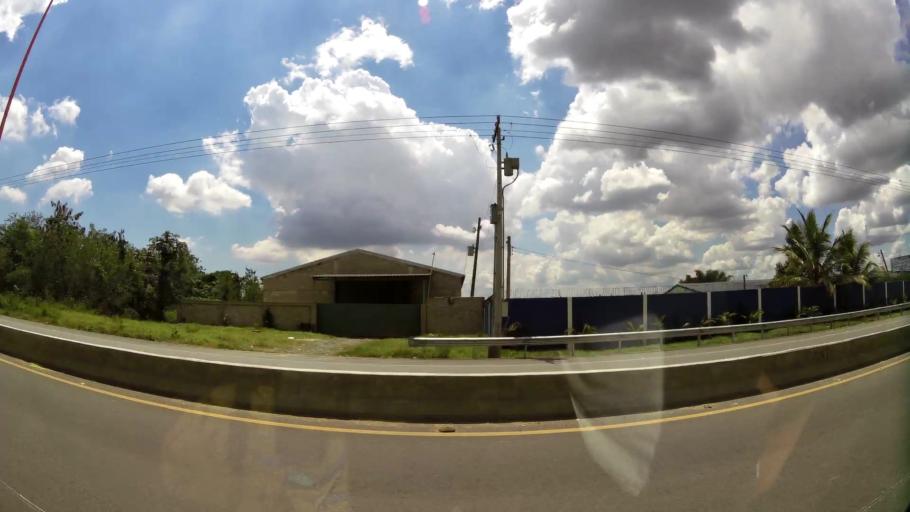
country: DO
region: Nacional
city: Santo Domingo
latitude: 18.5518
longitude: -69.9697
